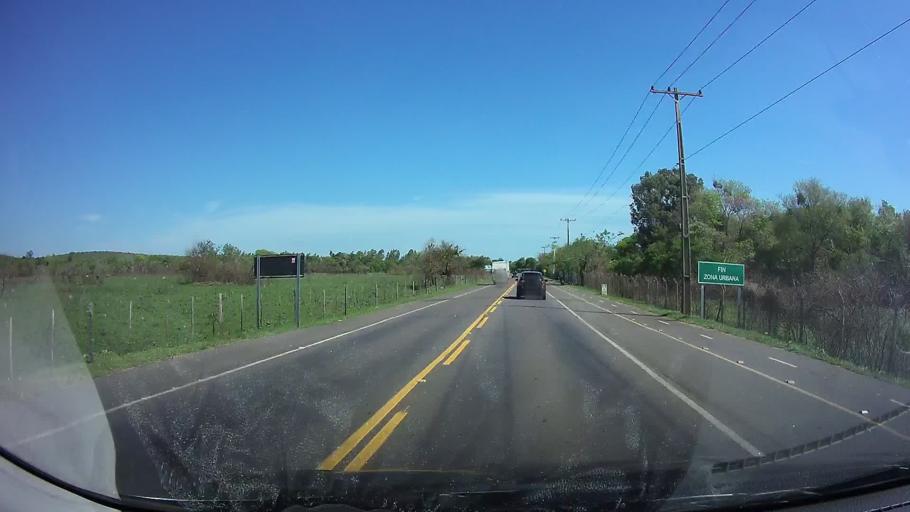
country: PY
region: Cordillera
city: San Bernardino
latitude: -25.2548
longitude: -57.3205
